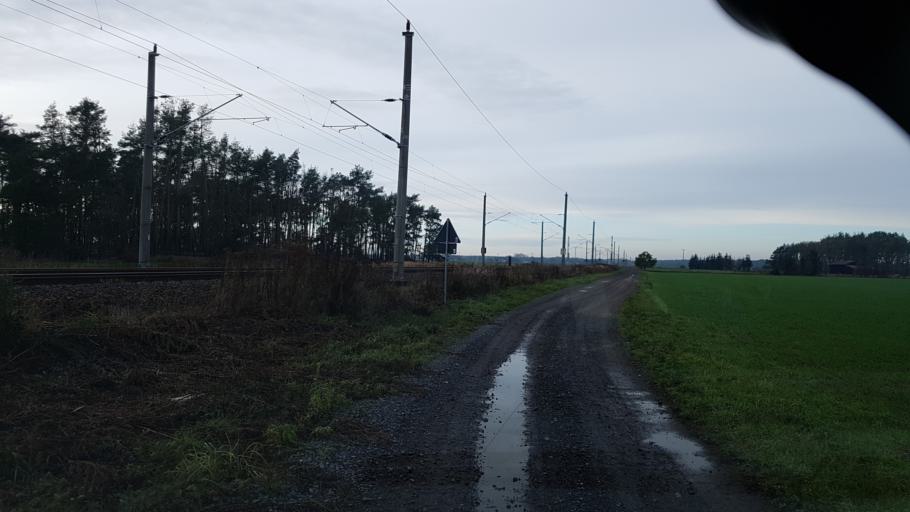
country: DE
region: Brandenburg
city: Bad Liebenwerda
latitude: 51.5469
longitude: 13.3188
